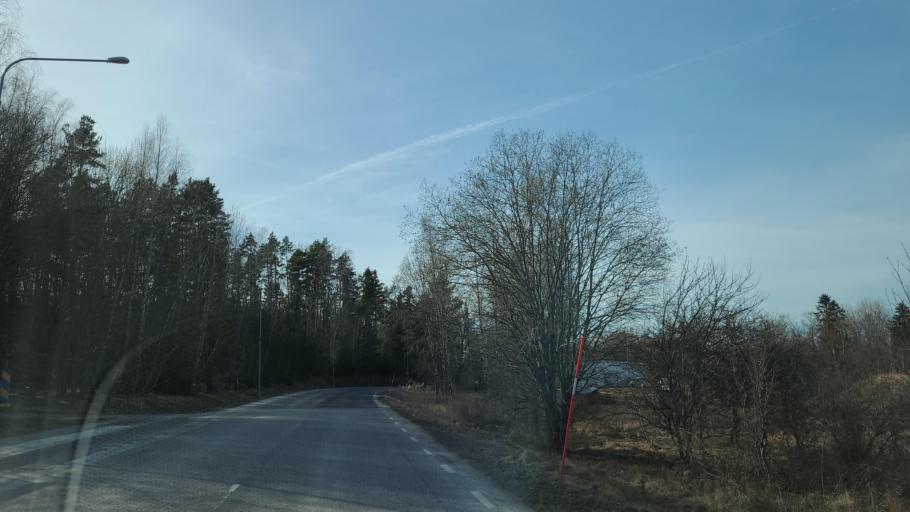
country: SE
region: Stockholm
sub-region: Ekero Kommun
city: Ekeroe
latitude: 59.2801
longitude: 17.7760
